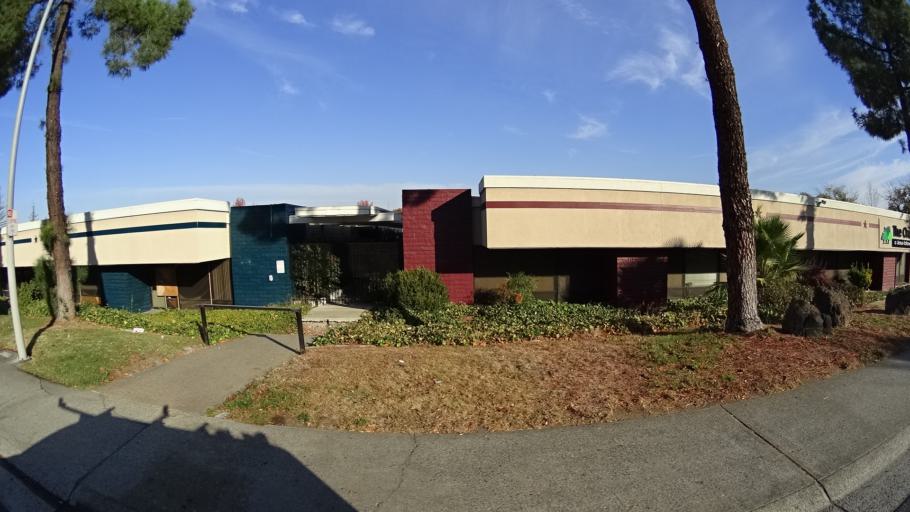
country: US
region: California
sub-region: Sacramento County
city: Foothill Farms
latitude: 38.6607
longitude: -121.3300
